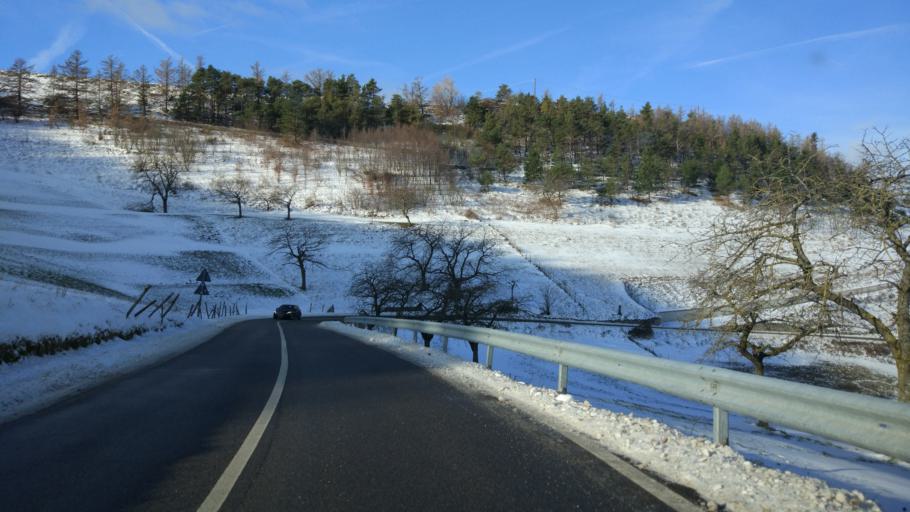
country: IT
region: Veneto
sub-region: Provincia di Verona
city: Sant'Anna d'Alfaedo
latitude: 45.6372
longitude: 10.9414
